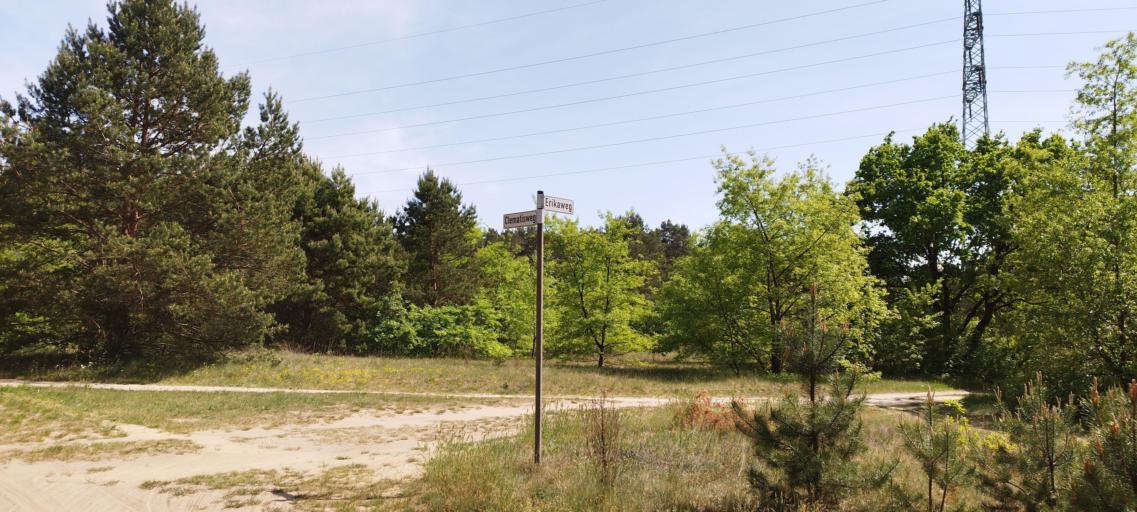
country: DE
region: Brandenburg
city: Rauen
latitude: 52.3746
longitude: 14.0141
